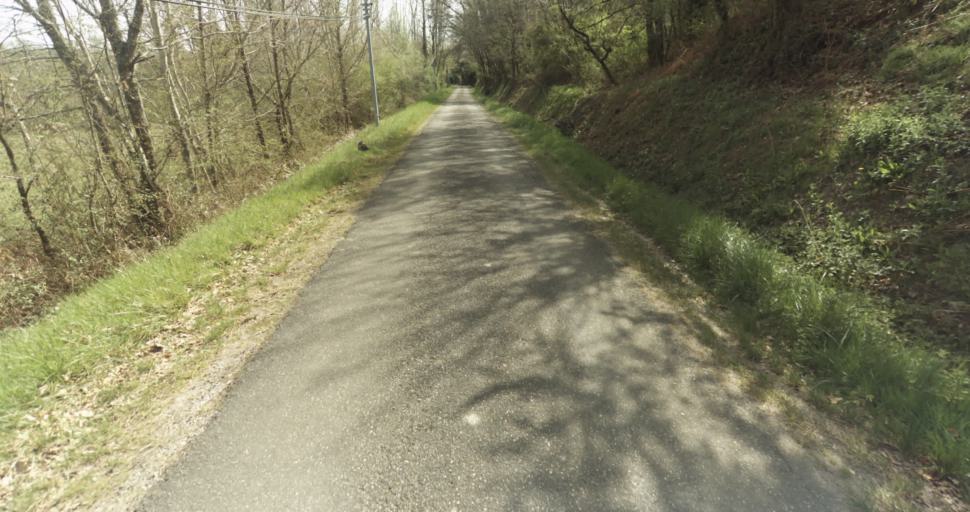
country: FR
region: Midi-Pyrenees
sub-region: Departement du Tarn-et-Garonne
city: Moissac
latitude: 44.1446
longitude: 1.0945
